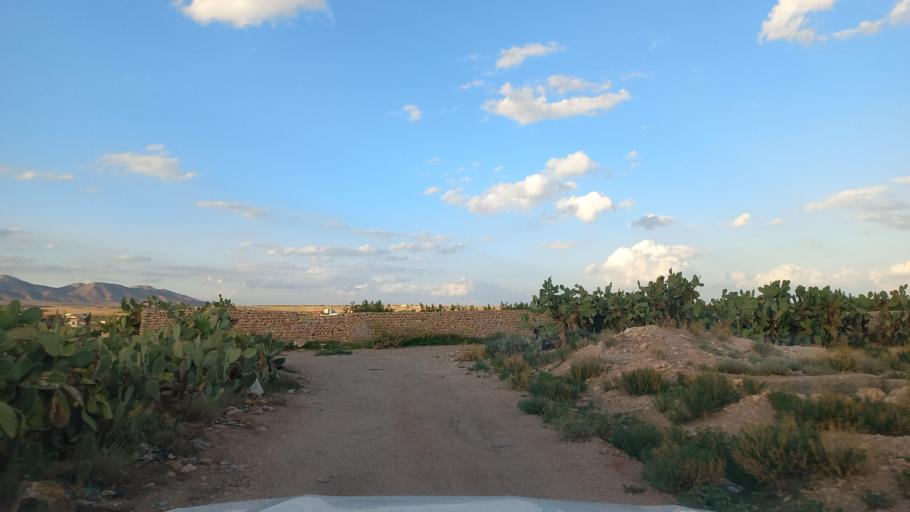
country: TN
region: Al Qasrayn
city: Sbiba
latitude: 35.3766
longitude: 9.0531
